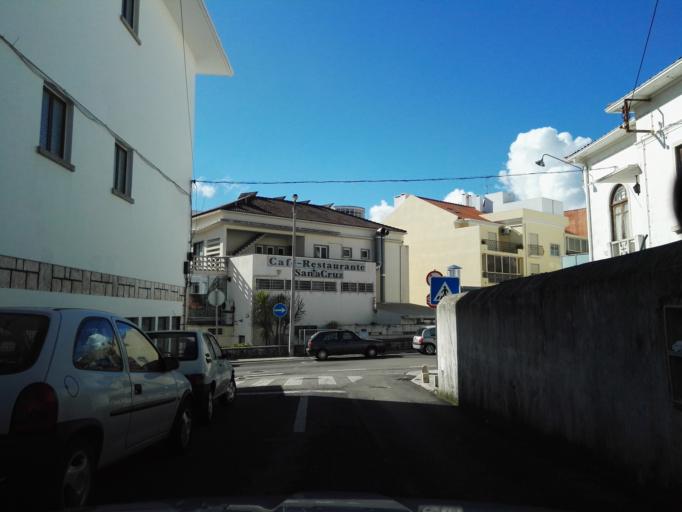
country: PT
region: Santarem
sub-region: Ourem
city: Fatima
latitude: 39.6321
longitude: -8.6758
